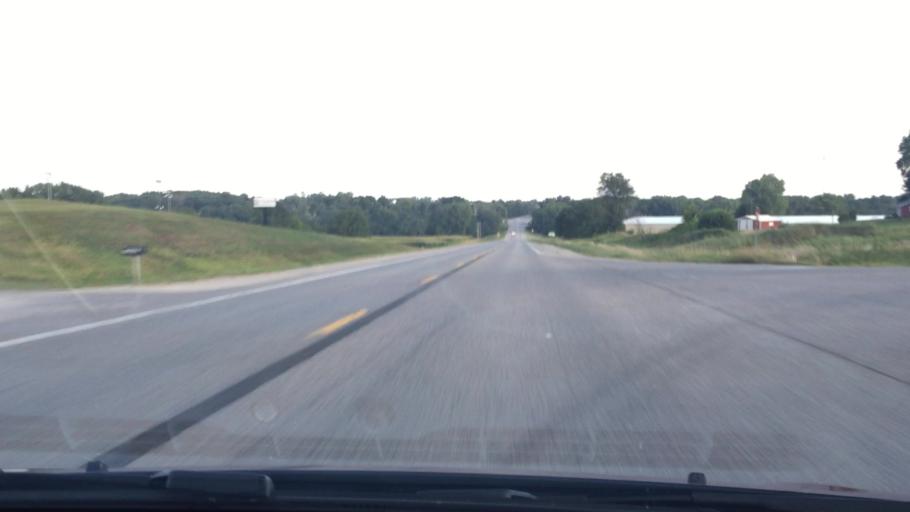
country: US
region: Iowa
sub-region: Muscatine County
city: Muscatine
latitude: 41.4665
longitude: -91.0347
